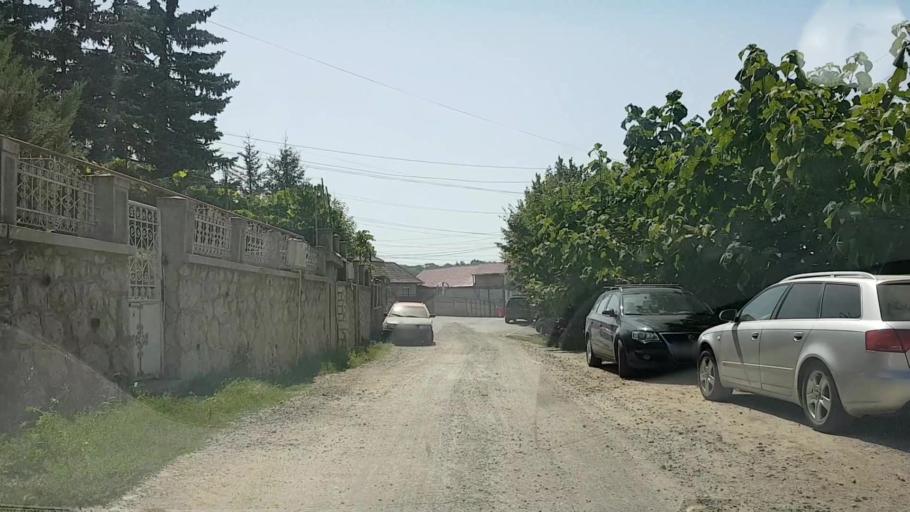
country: RO
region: Cluj
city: Turda
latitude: 46.5780
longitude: 23.7843
